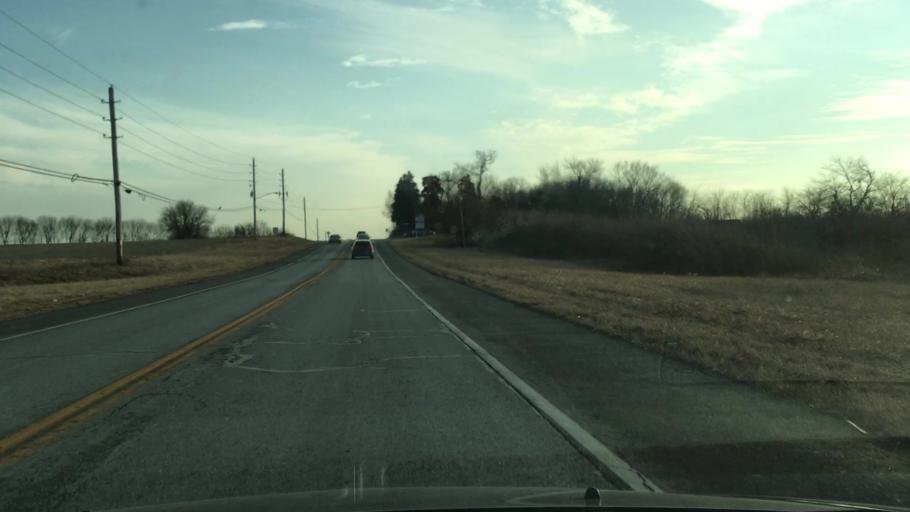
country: US
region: Missouri
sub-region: Jackson County
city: Lees Summit
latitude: 38.8827
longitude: -94.4155
